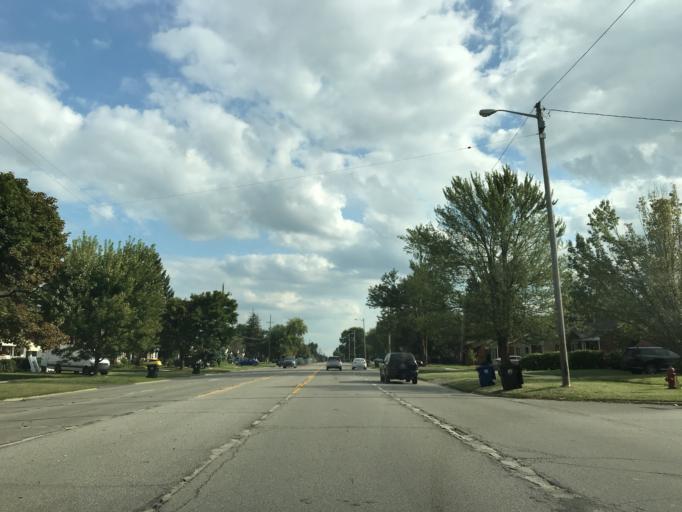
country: US
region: Michigan
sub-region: Wayne County
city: Redford
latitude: 42.4120
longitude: -83.2965
